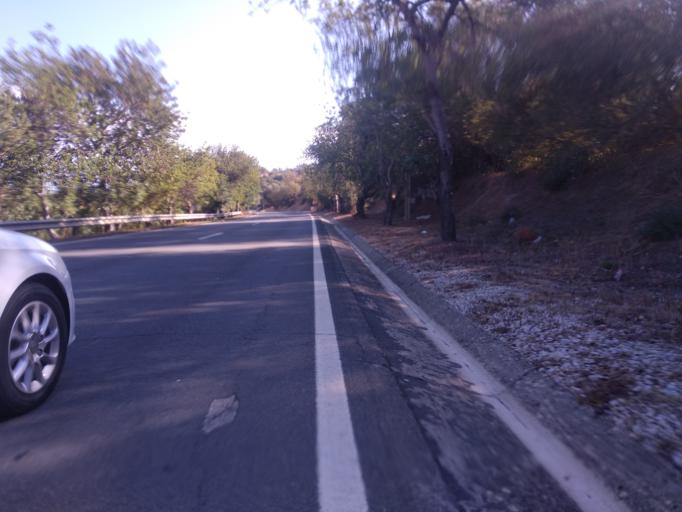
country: PT
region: Faro
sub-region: Sao Bras de Alportel
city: Sao Bras de Alportel
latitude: 37.1114
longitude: -7.9083
